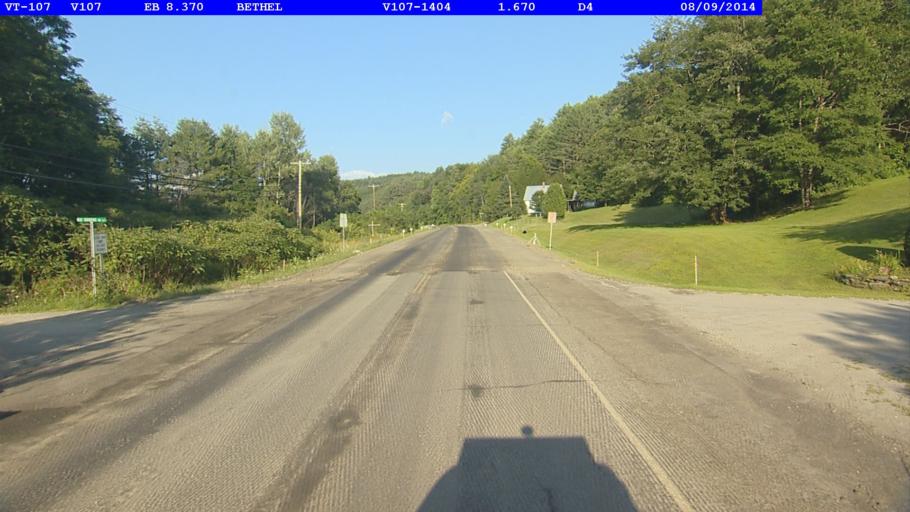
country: US
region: Vermont
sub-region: Orange County
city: Randolph
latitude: 43.8100
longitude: -72.6484
